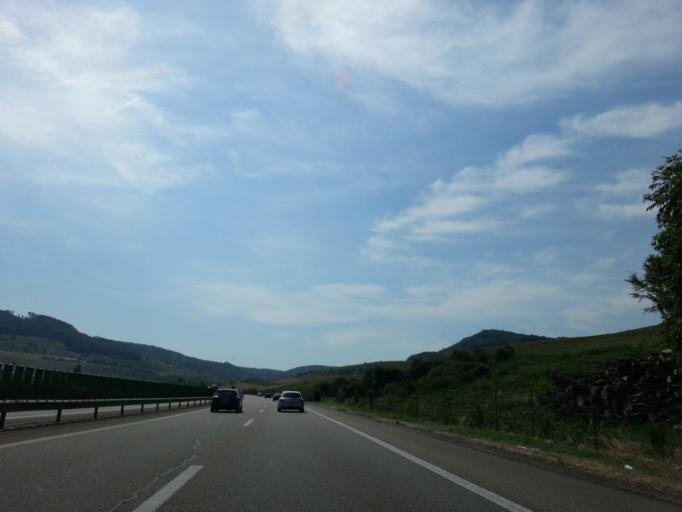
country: CH
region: Basel-Landschaft
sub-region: Bezirk Liestal
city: Arisdorf
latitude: 47.5195
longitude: 7.7536
